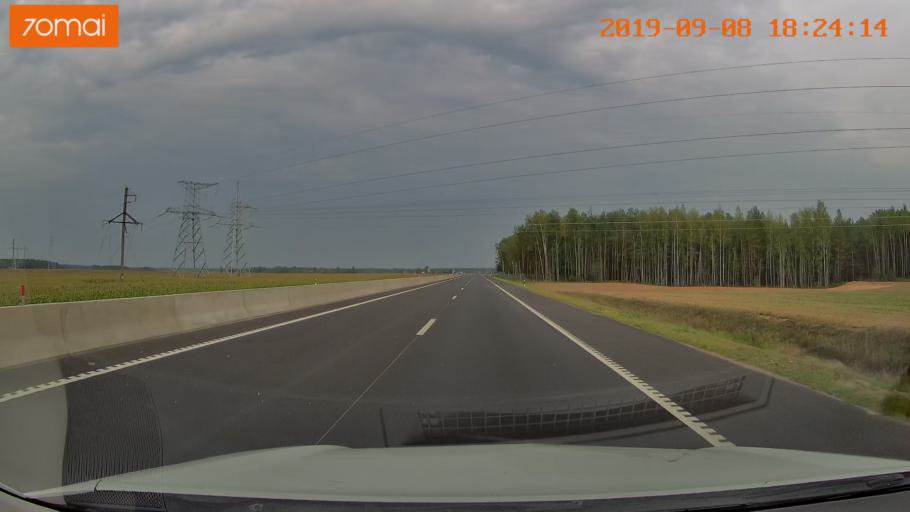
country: BY
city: Berezovka
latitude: 53.8425
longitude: 25.5323
